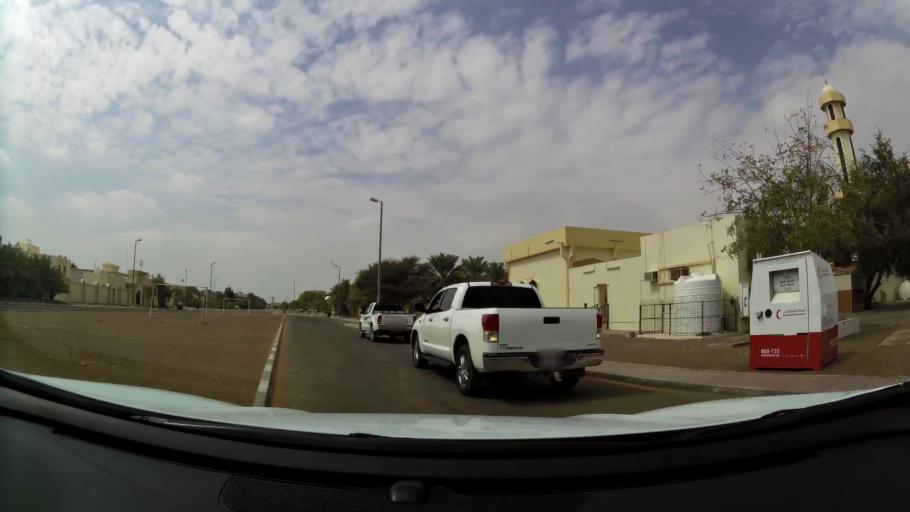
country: AE
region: Abu Dhabi
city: Al Ain
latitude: 24.2022
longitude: 55.8016
